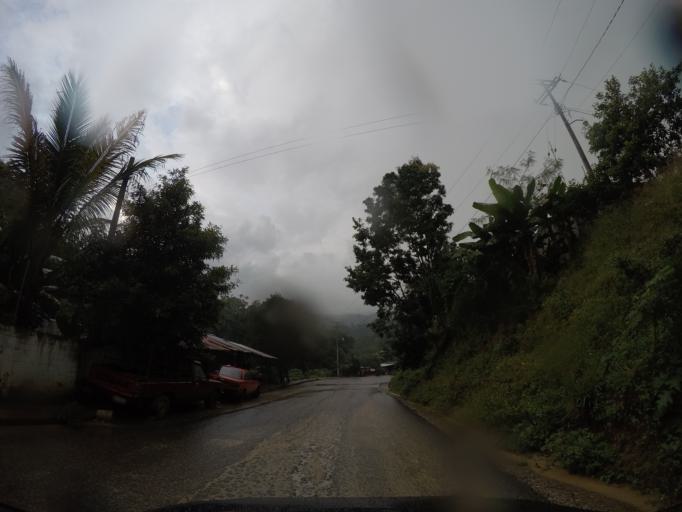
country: MX
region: Oaxaca
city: San Gabriel Mixtepec
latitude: 16.0896
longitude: -97.0801
